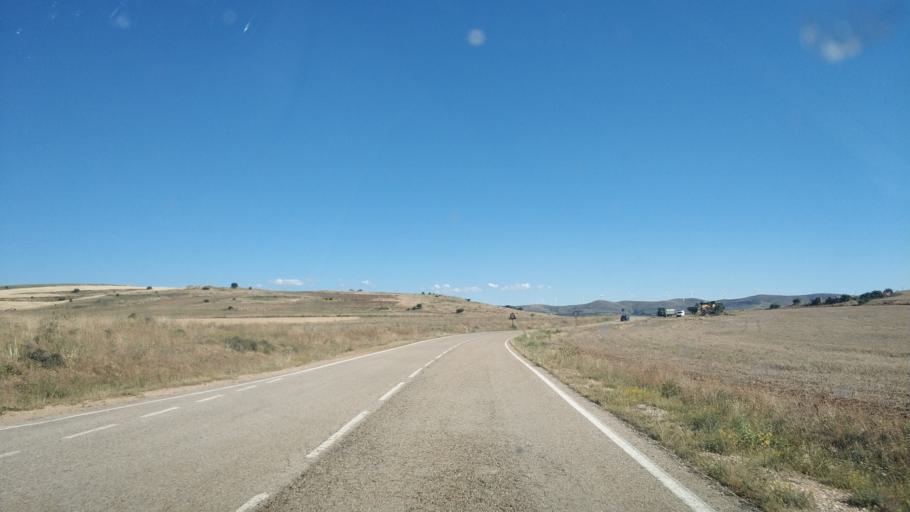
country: ES
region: Castille and Leon
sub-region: Provincia de Soria
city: Montejo de Tiermes
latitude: 41.3743
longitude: -3.1912
